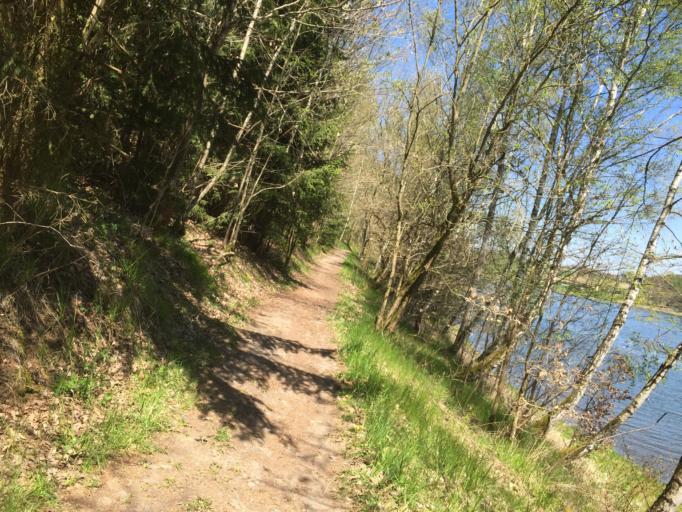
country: DE
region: Saxony
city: Neuensalz
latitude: 50.5211
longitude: 12.2059
